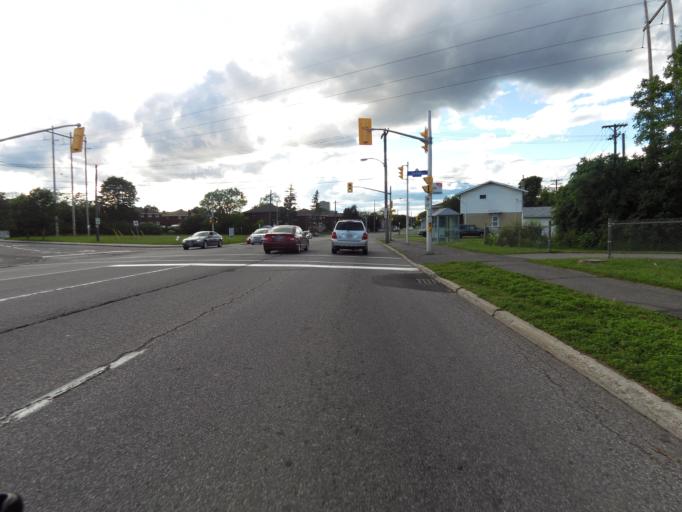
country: CA
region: Ontario
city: Ottawa
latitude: 45.3674
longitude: -75.7523
